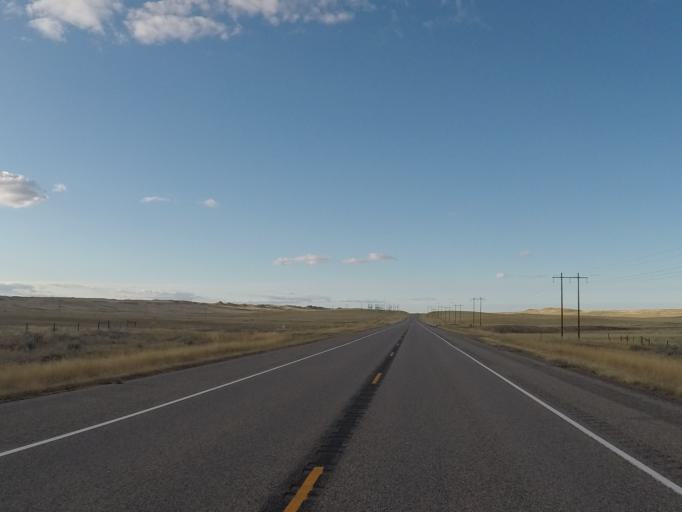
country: US
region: Montana
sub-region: Golden Valley County
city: Ryegate
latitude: 46.2072
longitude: -108.9217
